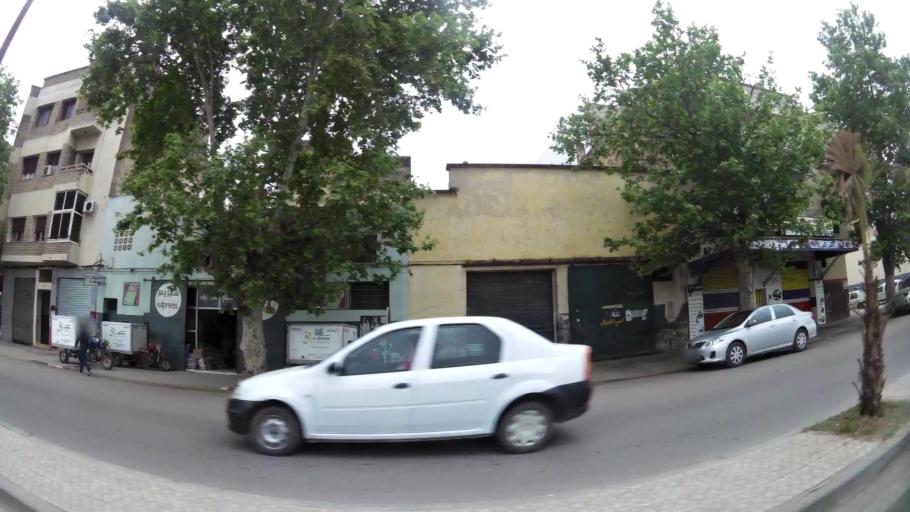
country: MA
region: Fes-Boulemane
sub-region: Fes
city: Fes
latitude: 34.0450
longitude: -5.0079
